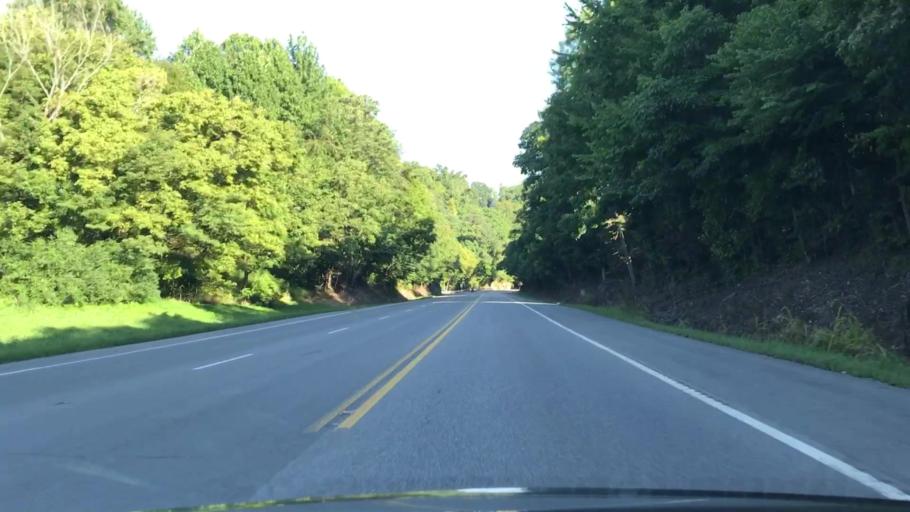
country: US
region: Tennessee
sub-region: Jackson County
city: Gainesboro
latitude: 36.3053
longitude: -85.6423
